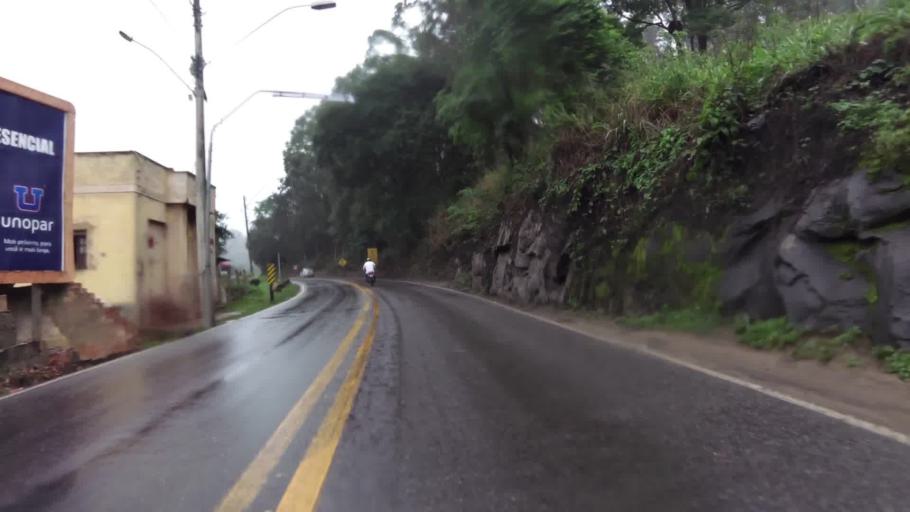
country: BR
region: Espirito Santo
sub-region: Iconha
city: Iconha
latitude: -20.7944
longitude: -40.8128
